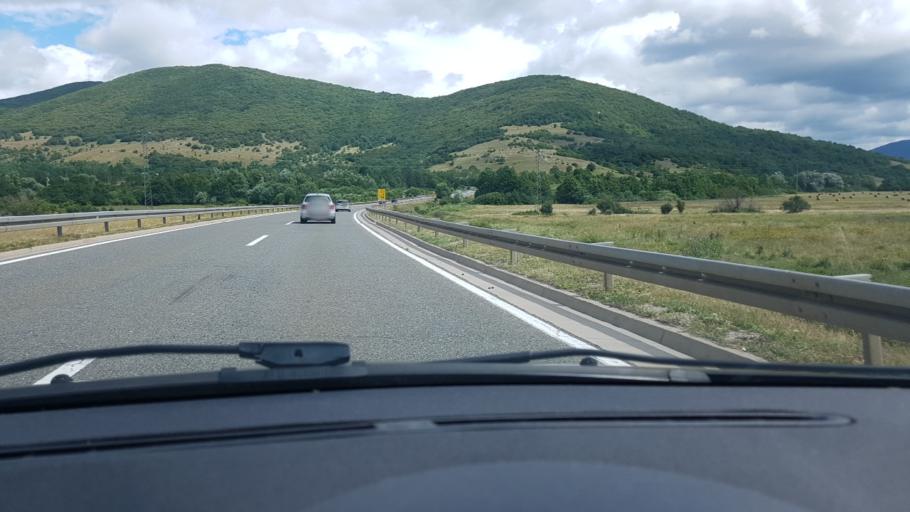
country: HR
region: Zadarska
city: Gracac
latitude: 44.5052
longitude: 15.7585
